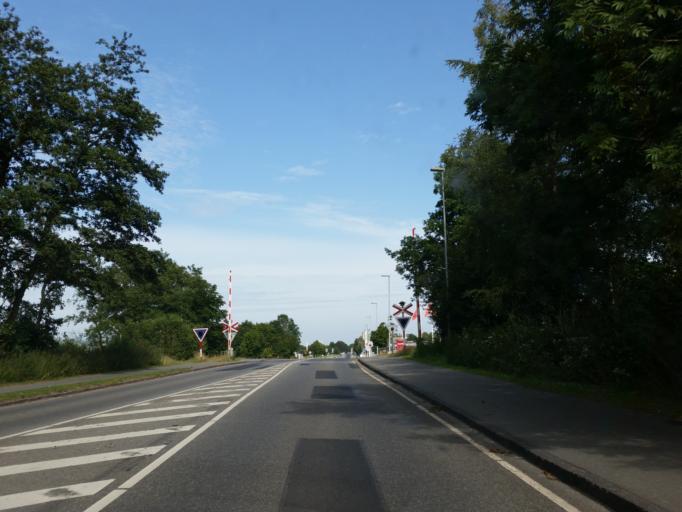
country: DK
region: South Denmark
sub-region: Tonder Kommune
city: Tonder
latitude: 54.9460
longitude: 8.8573
